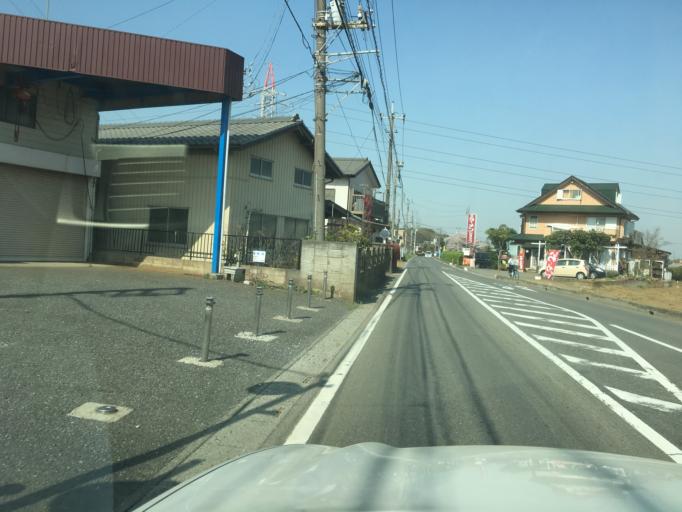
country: JP
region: Saitama
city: Sayama
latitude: 35.8471
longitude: 139.4479
